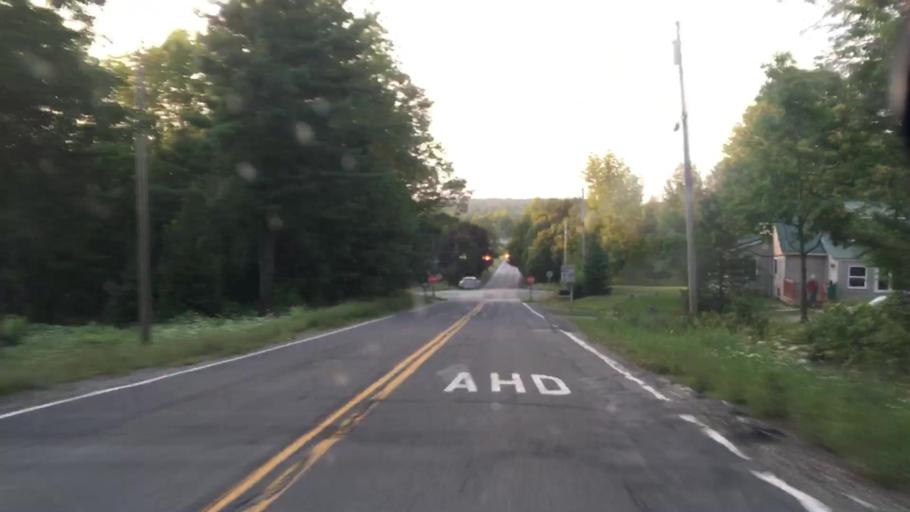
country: US
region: Maine
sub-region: Penobscot County
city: Hermon
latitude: 44.7341
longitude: -68.9632
